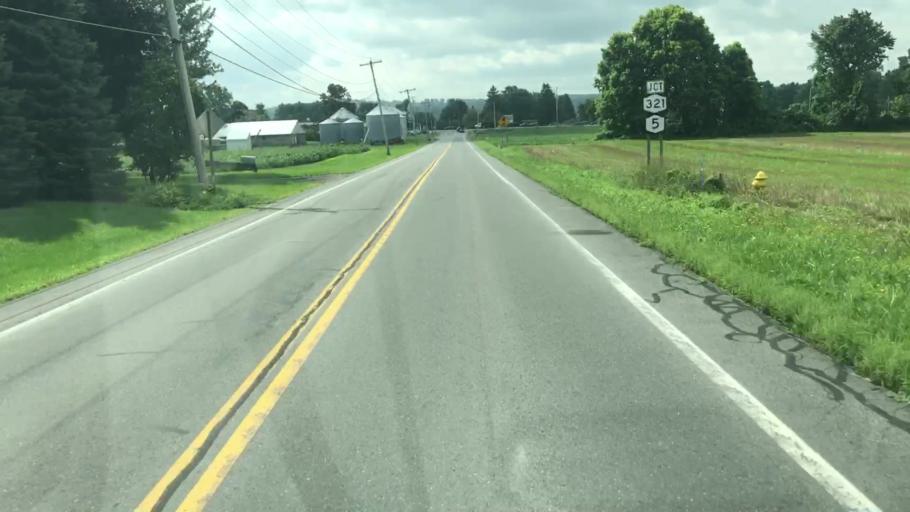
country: US
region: New York
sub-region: Onondaga County
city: Marcellus
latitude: 43.0379
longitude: -76.3656
